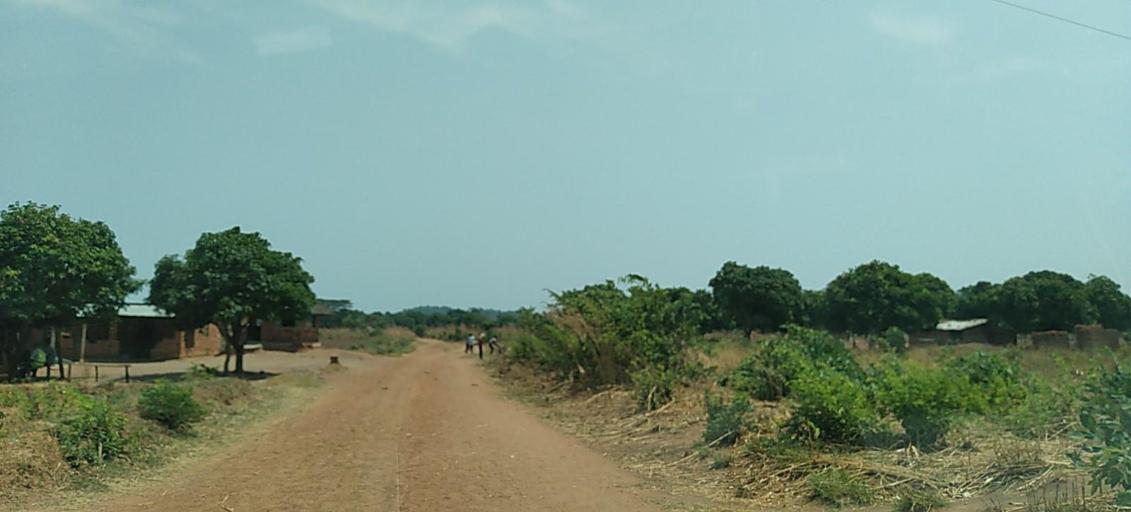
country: ZM
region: Copperbelt
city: Ndola
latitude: -13.0809
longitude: 28.7473
